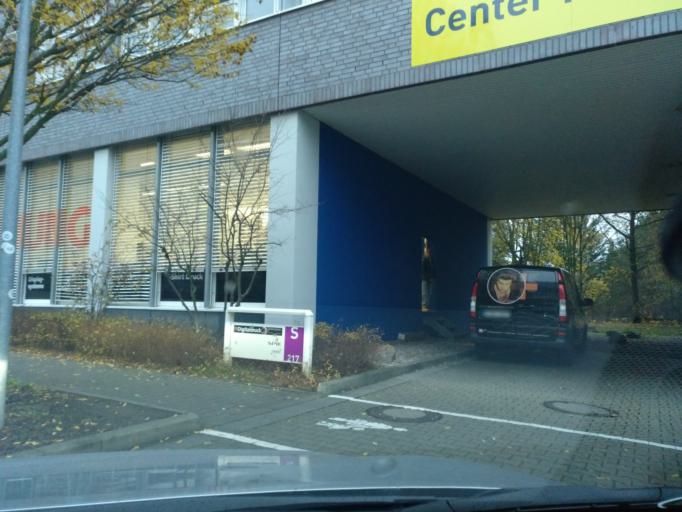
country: DE
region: Berlin
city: Mahlsdorf
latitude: 52.5068
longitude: 13.6220
